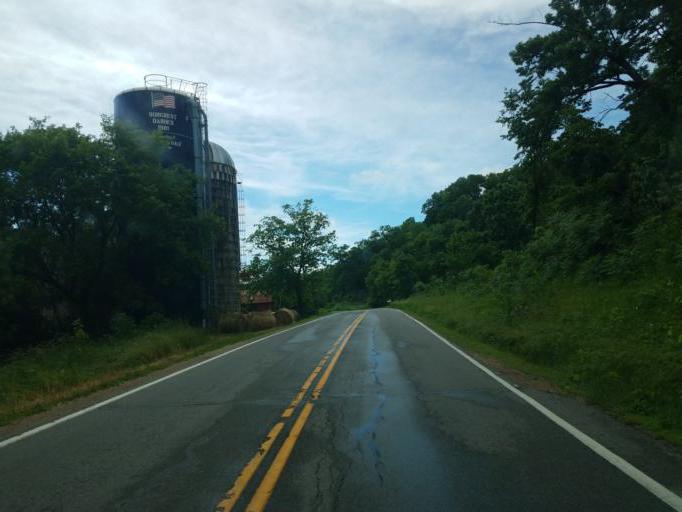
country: US
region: Wisconsin
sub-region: Vernon County
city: Hillsboro
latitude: 43.6609
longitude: -90.4333
